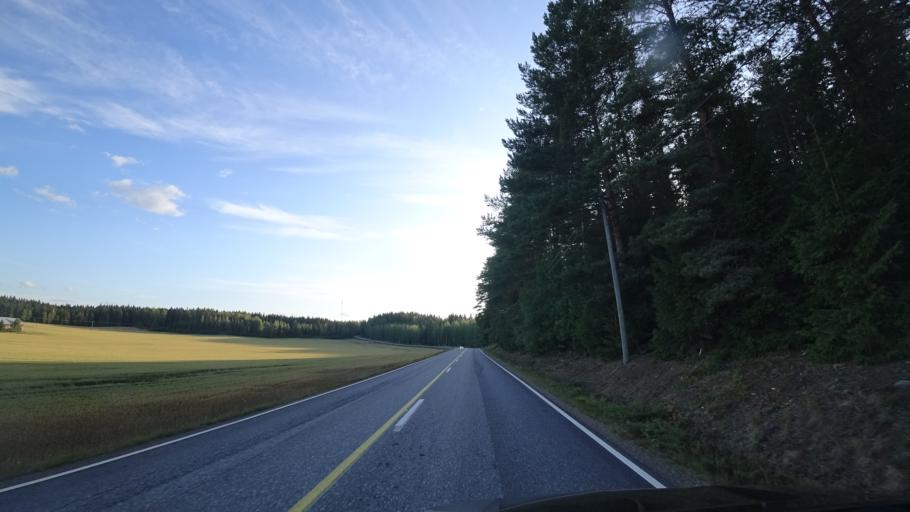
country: FI
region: Haeme
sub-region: Haemeenlinna
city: Lammi
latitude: 61.0186
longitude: 24.9111
